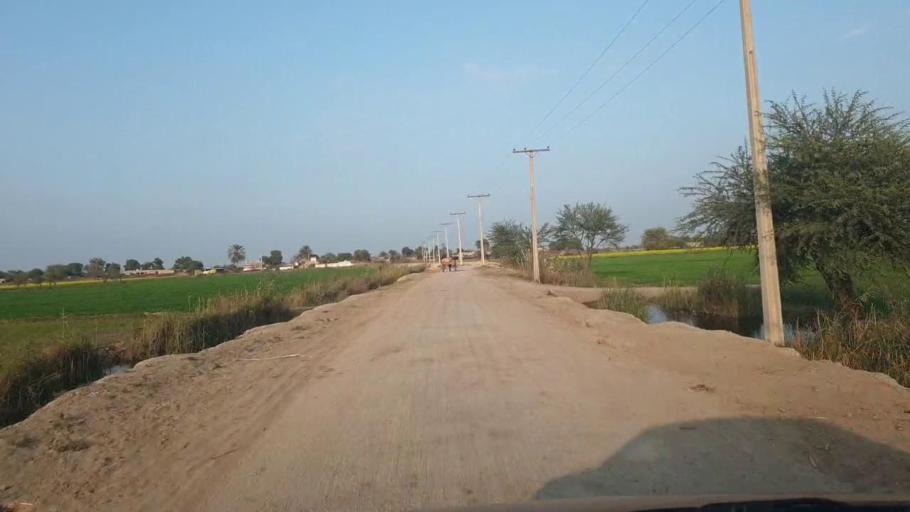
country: PK
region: Sindh
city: Berani
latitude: 25.8634
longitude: 68.7403
